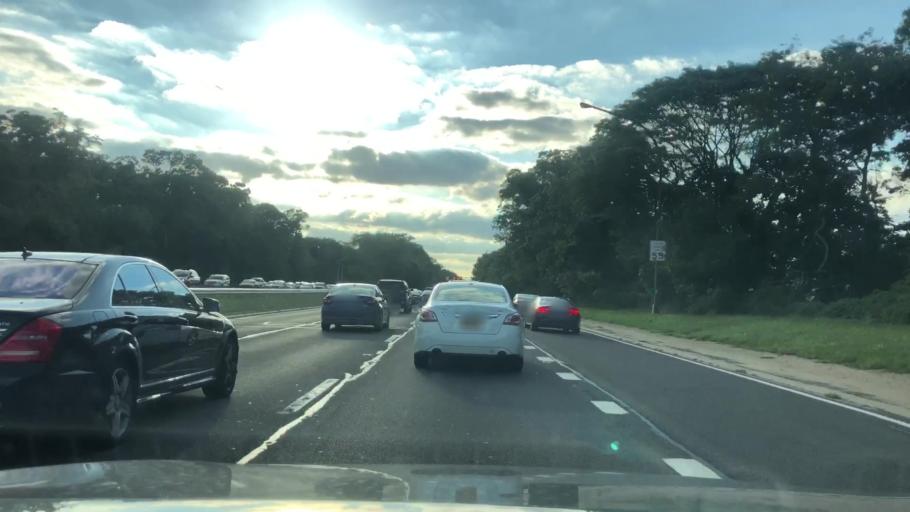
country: US
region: New York
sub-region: Nassau County
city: North Wantagh
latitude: 40.7012
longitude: -73.4960
